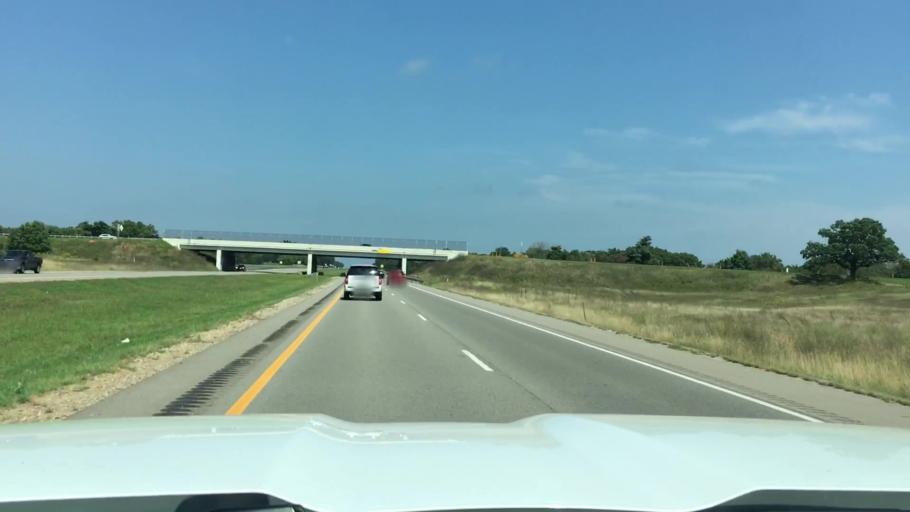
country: US
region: Michigan
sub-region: Kalamazoo County
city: Portage
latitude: 42.1976
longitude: -85.6459
